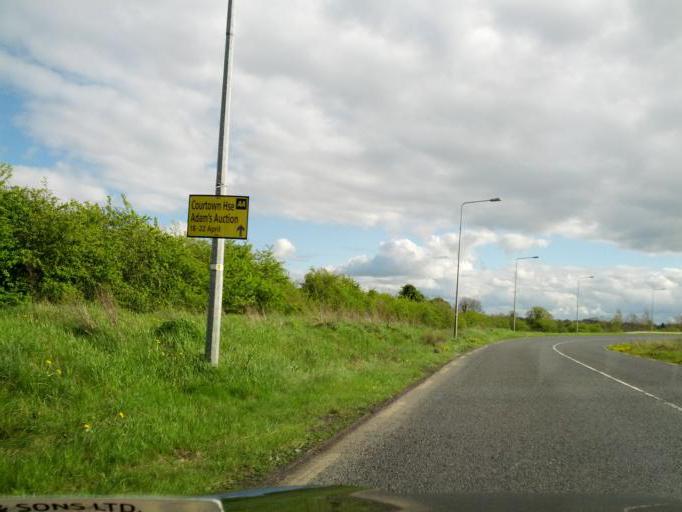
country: IE
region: Leinster
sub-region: Kildare
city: Kilcock
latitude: 53.4049
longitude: -6.6873
